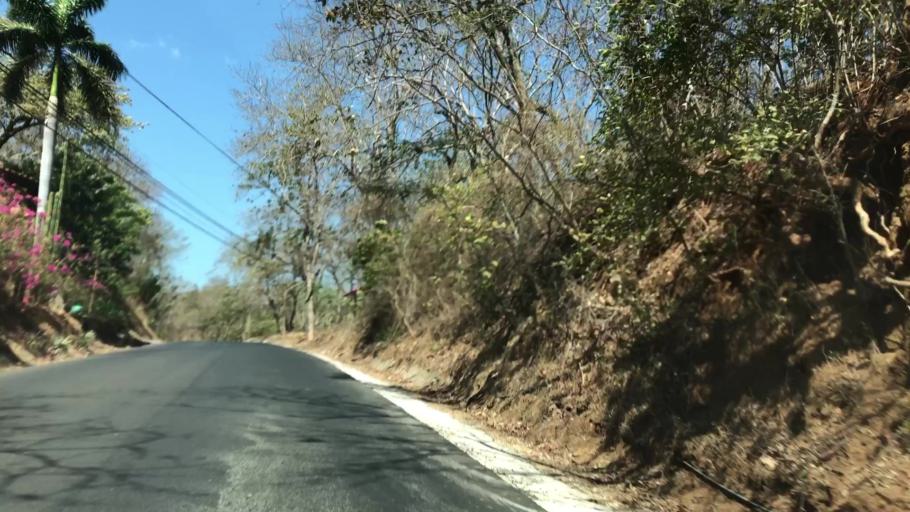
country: CR
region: Guanacaste
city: Sardinal
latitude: 10.3658
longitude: -85.7981
